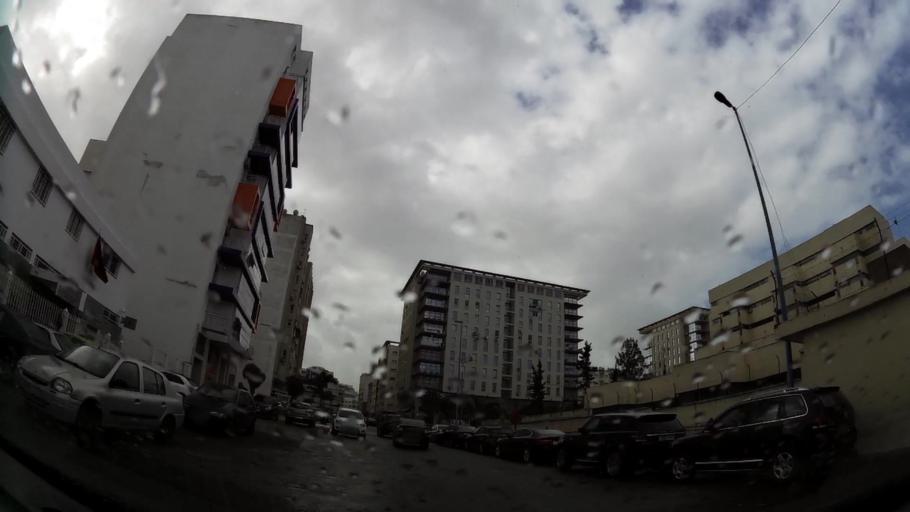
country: MA
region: Grand Casablanca
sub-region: Casablanca
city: Casablanca
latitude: 33.5947
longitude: -7.6018
